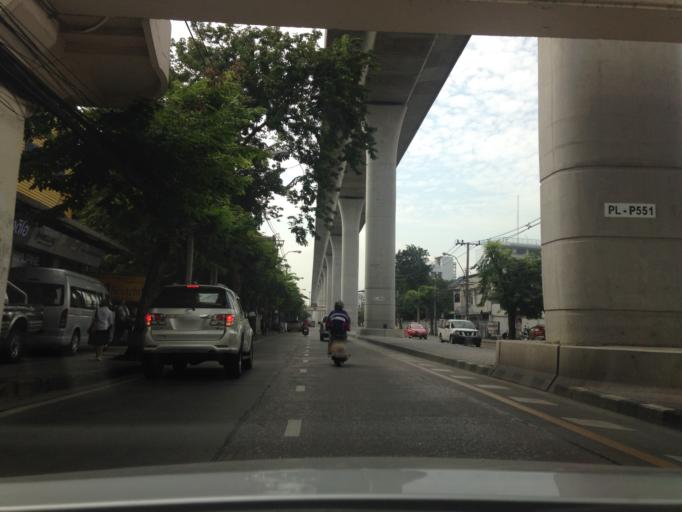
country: TH
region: Bangkok
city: Bang Sue
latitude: 13.8171
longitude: 100.5327
